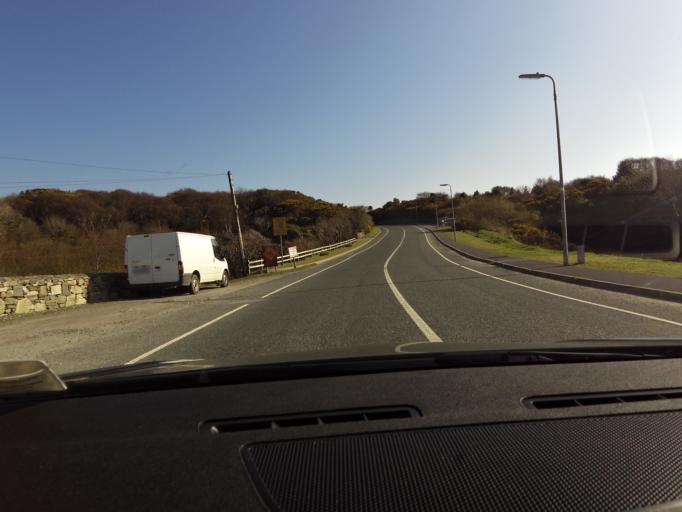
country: IE
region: Connaught
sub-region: County Galway
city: Clifden
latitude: 53.4846
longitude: -10.0240
